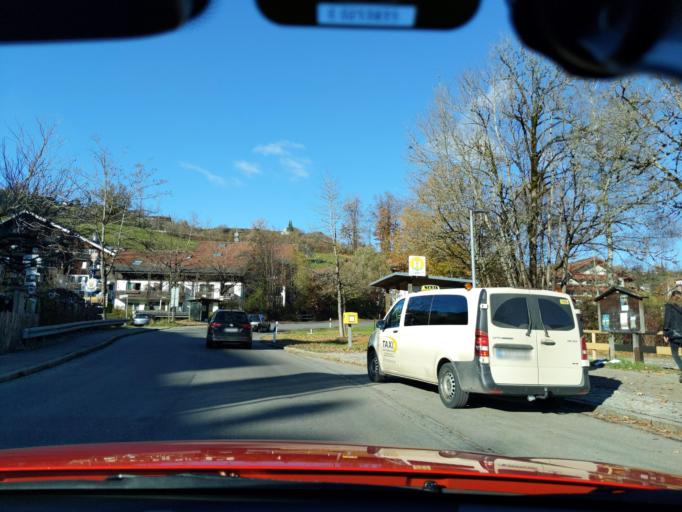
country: DE
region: Bavaria
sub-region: Swabia
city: Oberstaufen
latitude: 47.5454
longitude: 10.0197
